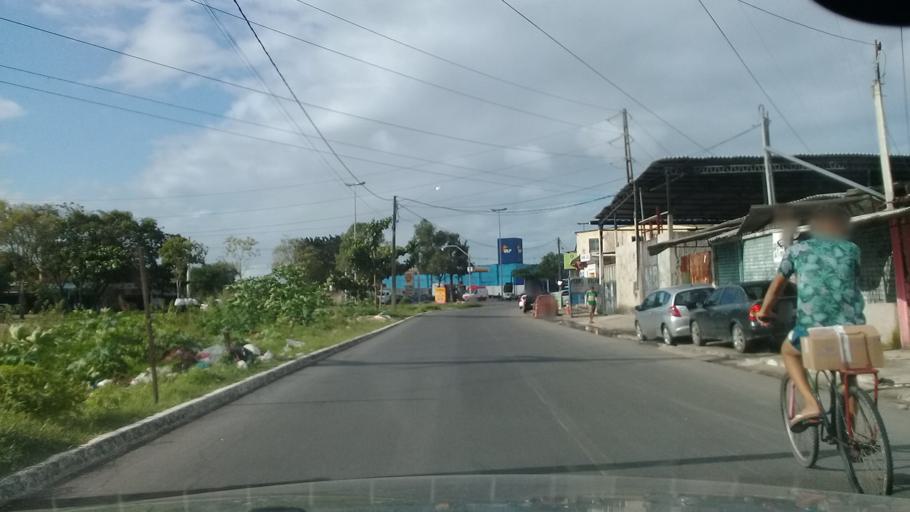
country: BR
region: Pernambuco
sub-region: Recife
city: Recife
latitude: -8.0659
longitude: -34.9388
